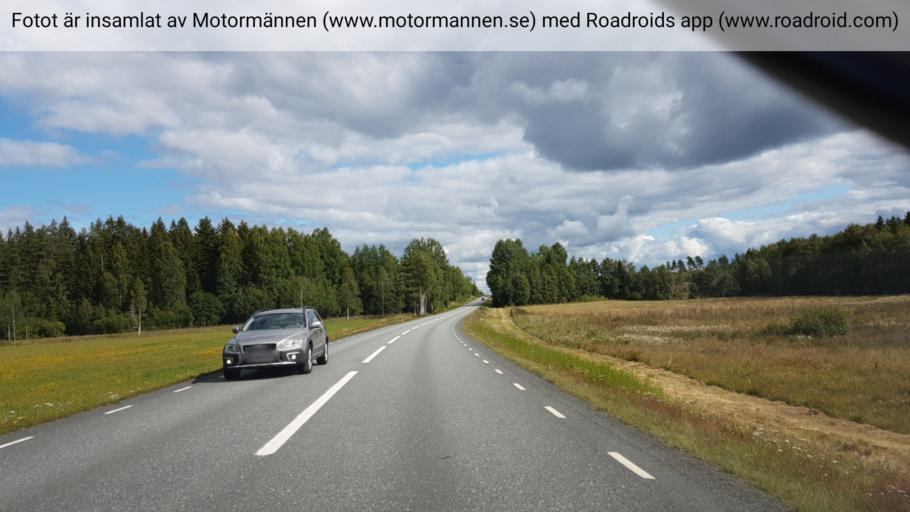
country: SE
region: Joenkoeping
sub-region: Aneby Kommun
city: Aneby
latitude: 57.8012
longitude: 14.7018
